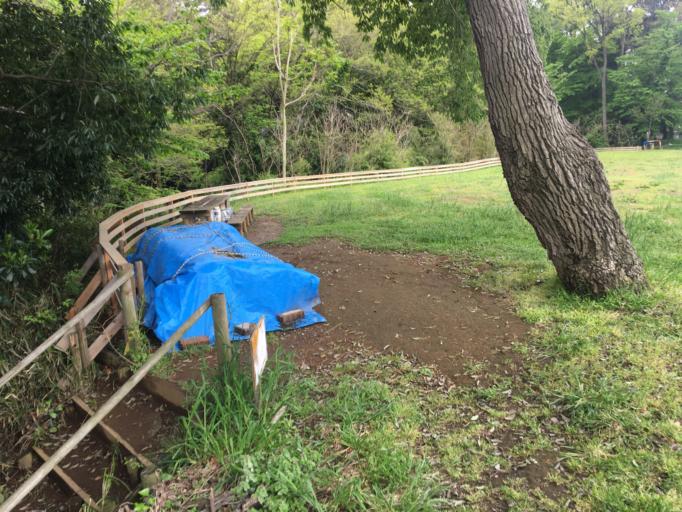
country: JP
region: Saitama
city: Oi
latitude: 35.8544
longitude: 139.5462
